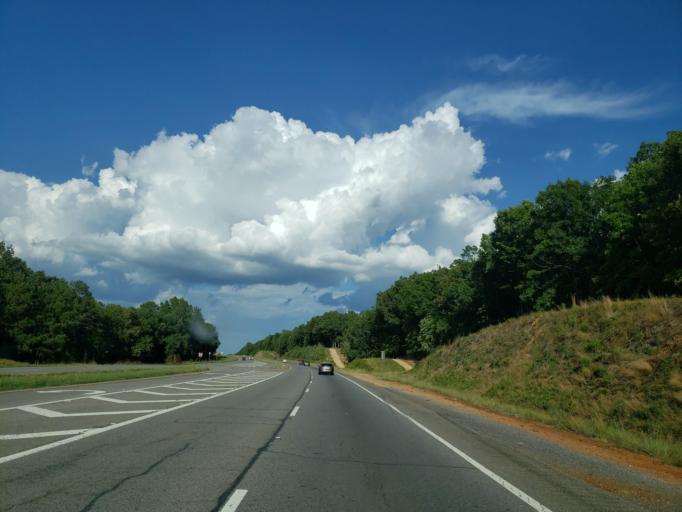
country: US
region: Georgia
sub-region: Bartow County
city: Euharlee
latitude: 34.2110
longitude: -84.9632
